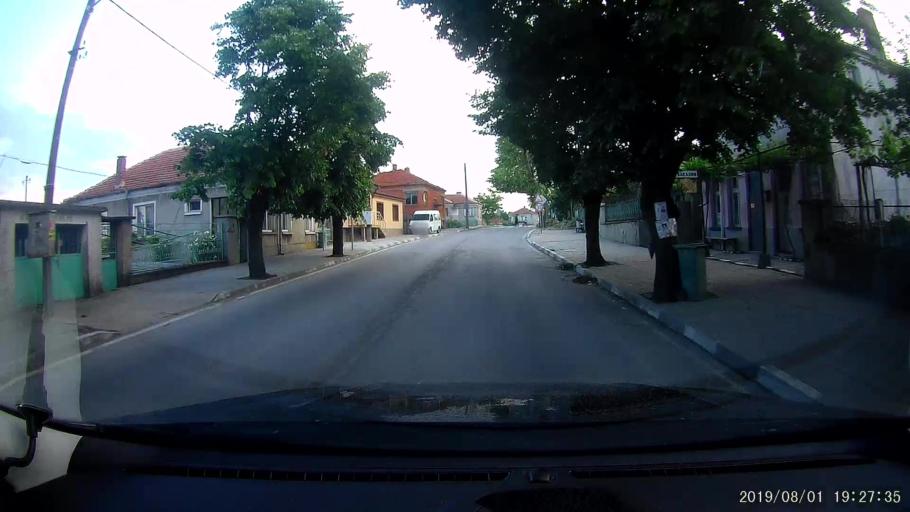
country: BG
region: Burgas
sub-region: Obshtina Sungurlare
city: Sungurlare
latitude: 42.8500
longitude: 26.9295
